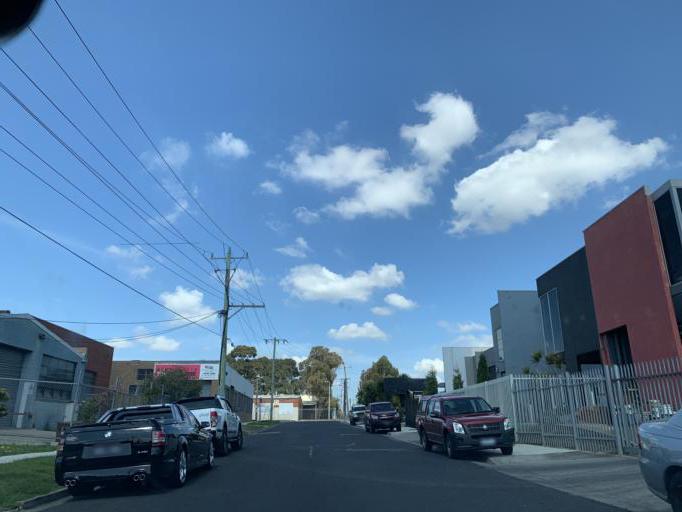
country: AU
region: Victoria
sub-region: Moreland
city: Coburg North
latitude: -37.7285
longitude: 144.9589
